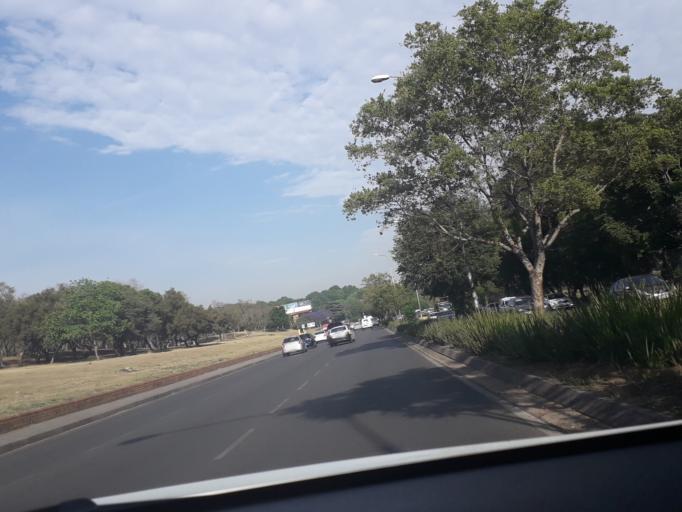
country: ZA
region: Gauteng
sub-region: City of Johannesburg Metropolitan Municipality
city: Johannesburg
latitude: -26.1005
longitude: 28.0364
